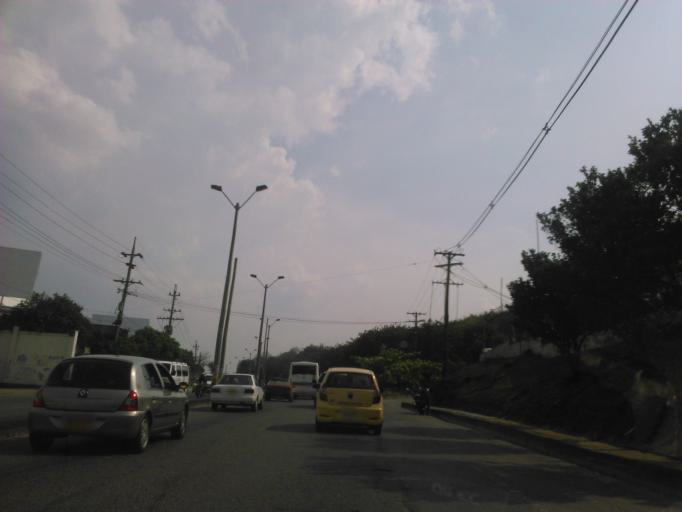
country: CO
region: Antioquia
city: Bello
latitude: 6.3088
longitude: -75.5601
